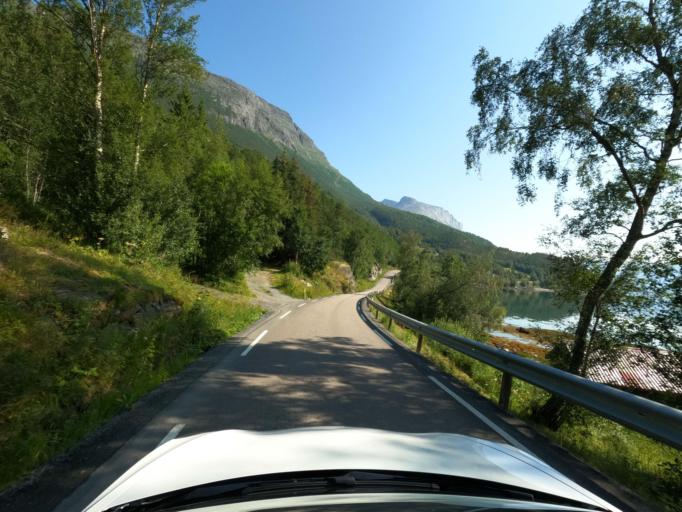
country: NO
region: Nordland
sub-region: Narvik
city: Narvik
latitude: 68.2982
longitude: 17.3491
